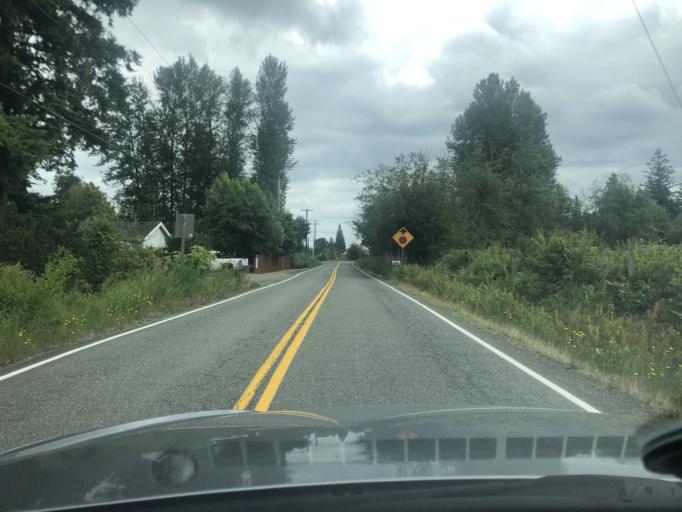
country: US
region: Washington
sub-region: King County
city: Lea Hill
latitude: 47.3020
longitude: -122.1456
